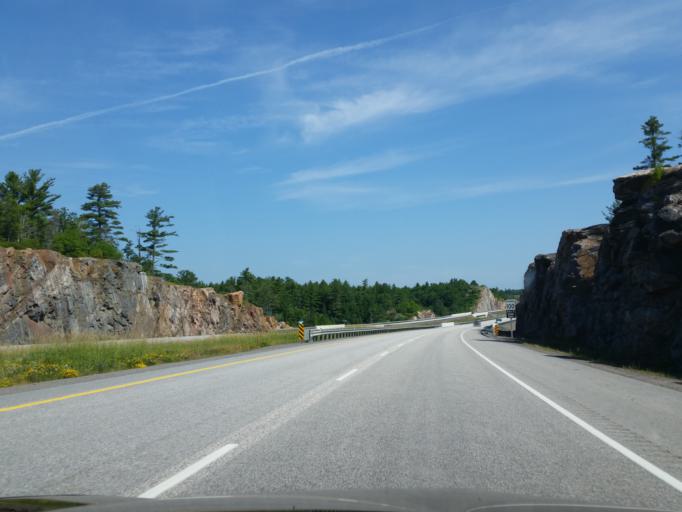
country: CA
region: Ontario
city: Greater Sudbury
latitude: 46.2113
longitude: -80.7686
